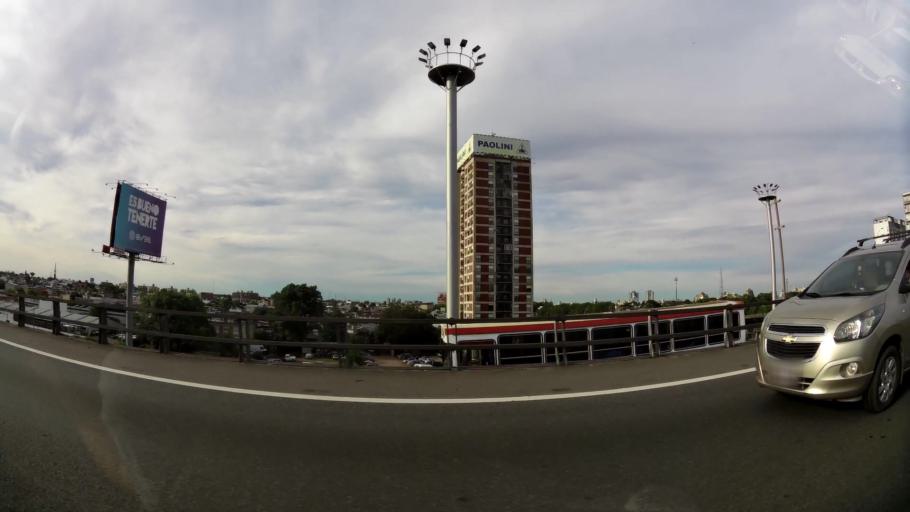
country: AR
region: Buenos Aires
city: Caseros
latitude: -34.6346
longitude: -58.5310
